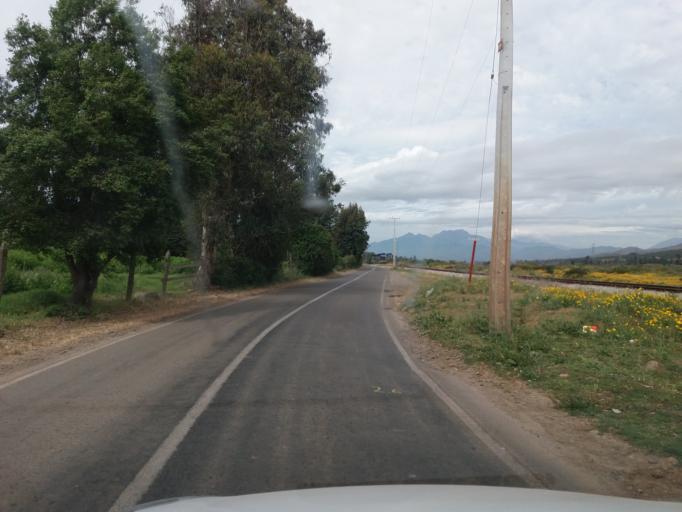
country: CL
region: Valparaiso
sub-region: Provincia de Marga Marga
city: Quilpue
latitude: -32.9162
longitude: -71.4180
